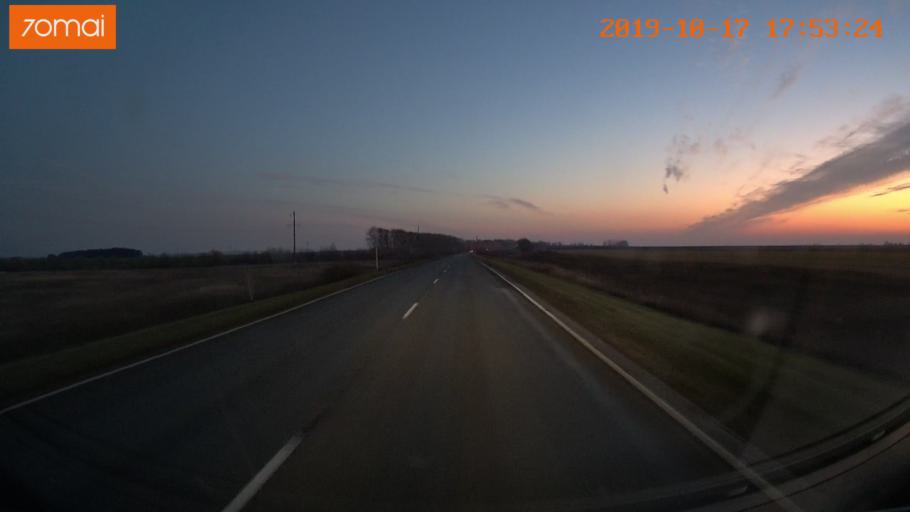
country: RU
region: Tula
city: Kurkino
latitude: 53.6202
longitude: 38.6783
